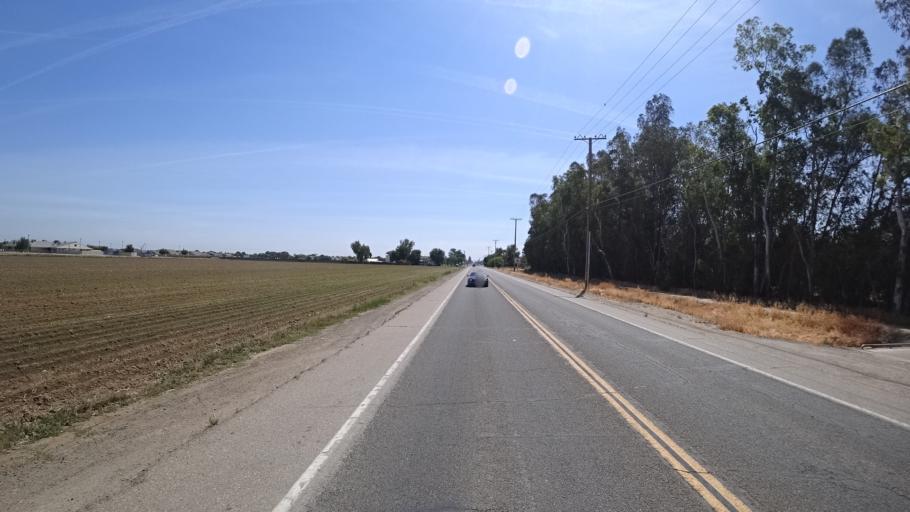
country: US
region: California
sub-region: Kings County
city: Armona
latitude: 36.3426
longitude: -119.6884
